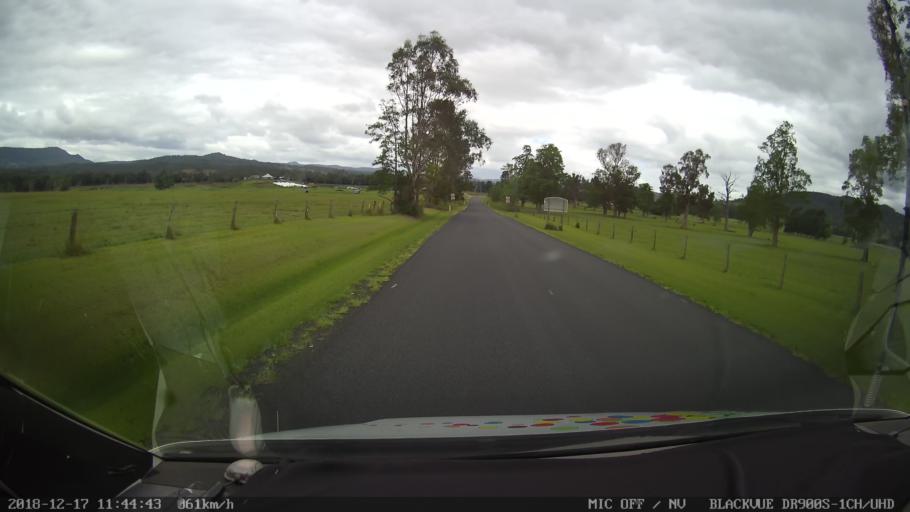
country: AU
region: New South Wales
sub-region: Kyogle
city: Kyogle
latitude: -28.6507
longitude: 152.5951
